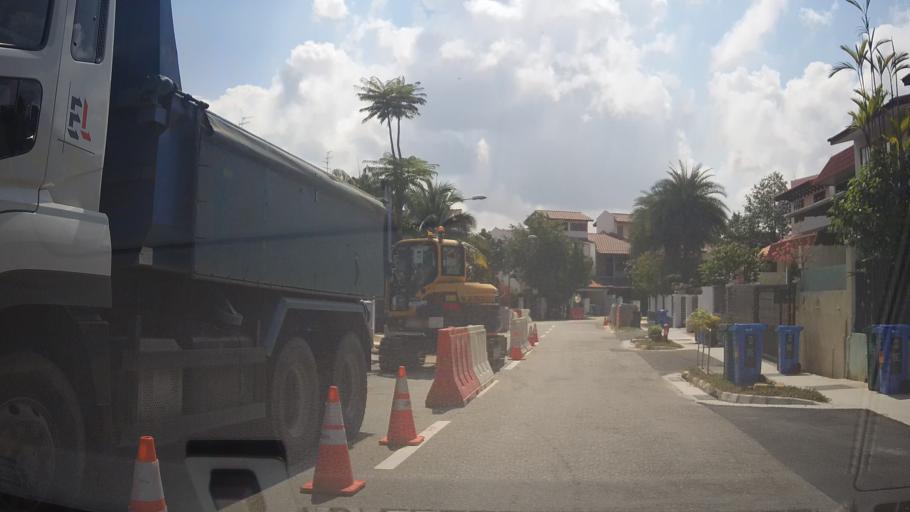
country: MY
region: Johor
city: Kampung Pasir Gudang Baru
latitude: 1.3815
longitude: 103.9432
